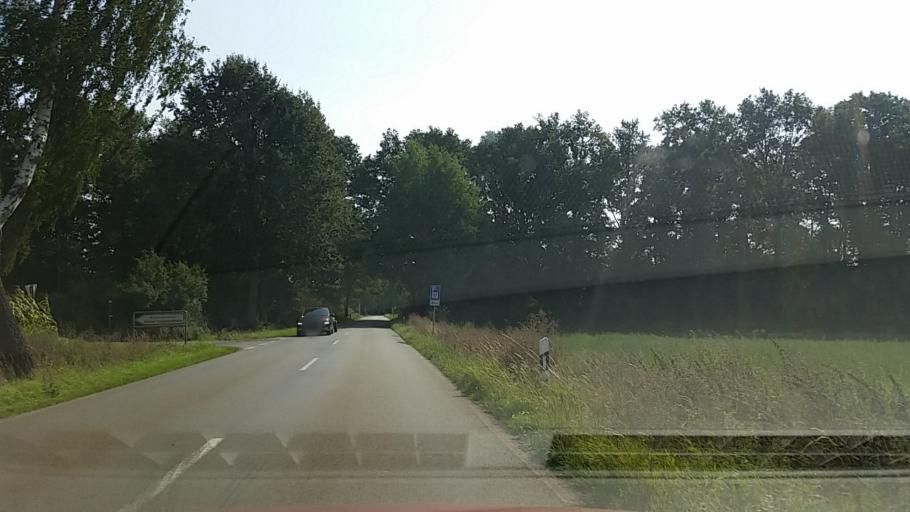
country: DE
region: Mecklenburg-Vorpommern
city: Domitz
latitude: 53.1278
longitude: 11.2363
